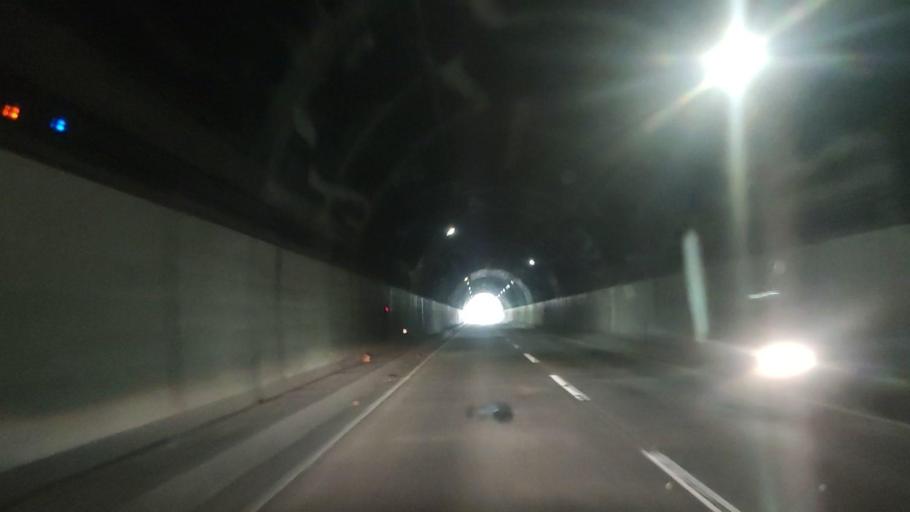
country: JP
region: Kagoshima
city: Okuchi-shinohara
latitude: 31.9729
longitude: 130.7408
